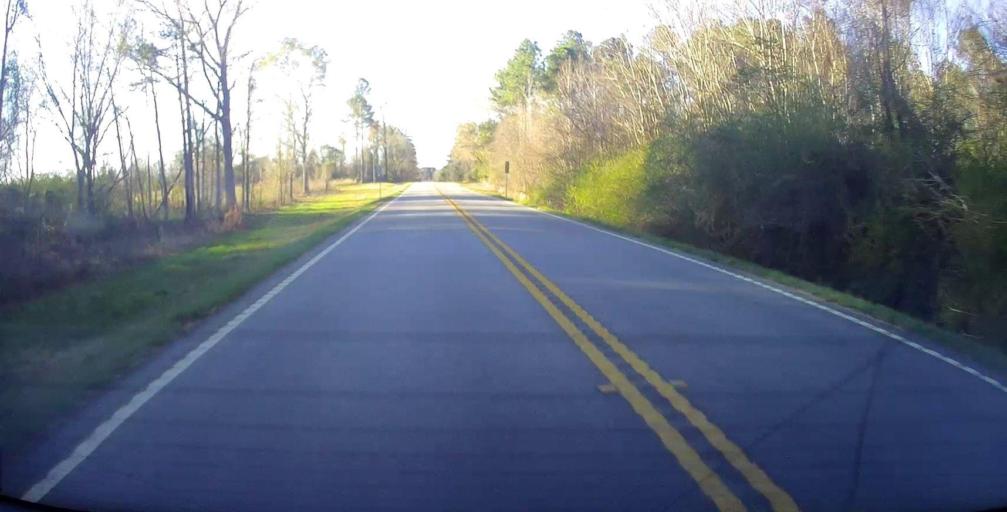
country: US
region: Georgia
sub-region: Wilcox County
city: Abbeville
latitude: 32.1283
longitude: -83.3339
